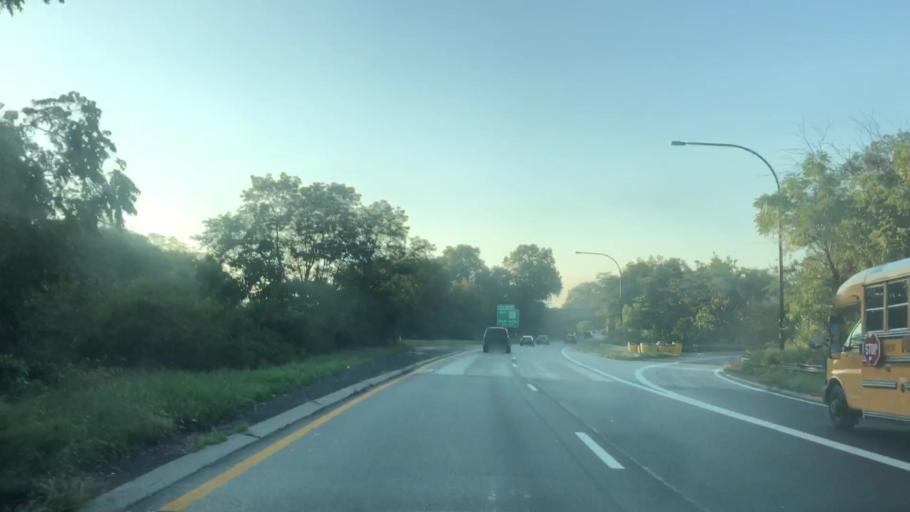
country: US
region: New York
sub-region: Nassau County
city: North Bellmore
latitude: 40.7017
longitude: -73.5213
